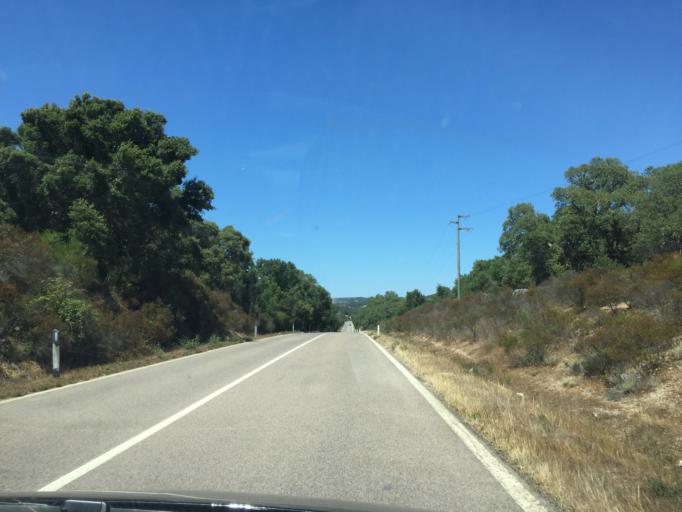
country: IT
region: Sardinia
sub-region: Provincia di Olbia-Tempio
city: Aggius
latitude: 40.9628
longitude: 9.0954
